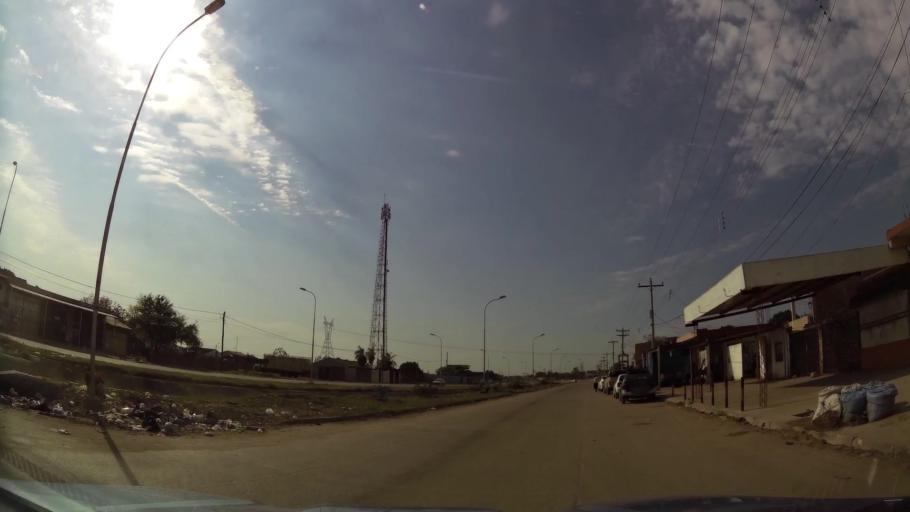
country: BO
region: Santa Cruz
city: Santa Cruz de la Sierra
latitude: -17.7271
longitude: -63.1383
